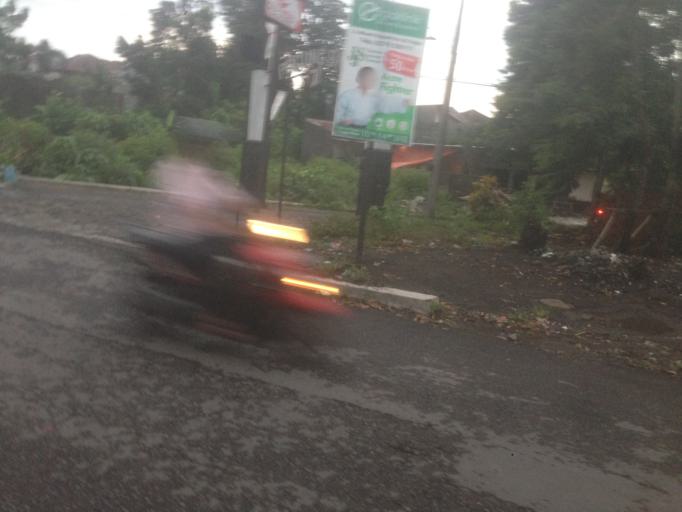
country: ID
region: Daerah Istimewa Yogyakarta
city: Melati
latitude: -7.7558
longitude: 110.3774
